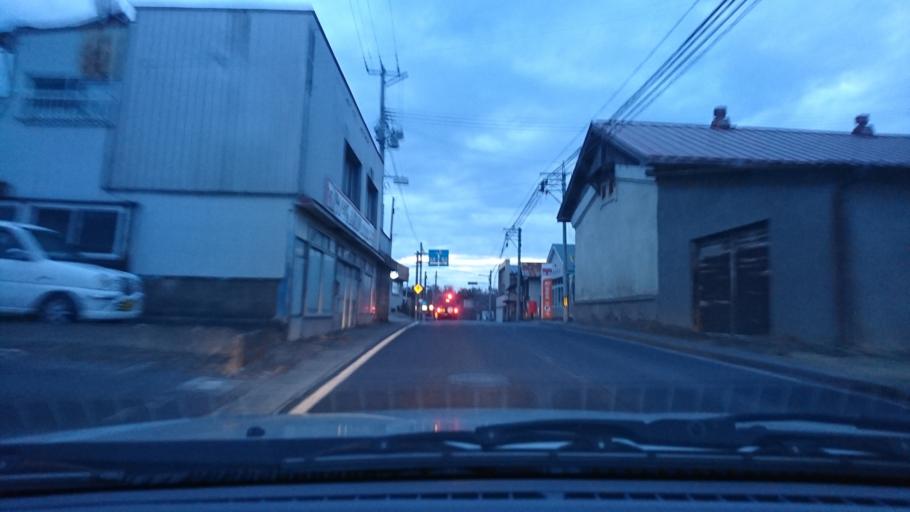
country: JP
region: Iwate
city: Ichinoseki
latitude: 38.7813
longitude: 141.2241
